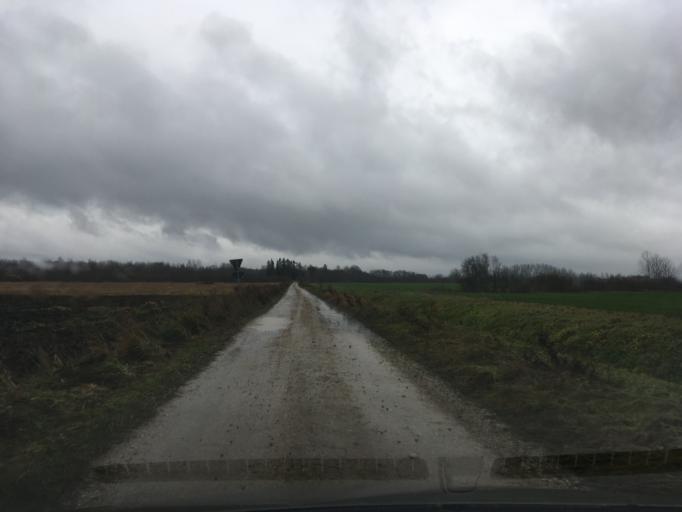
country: EE
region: Laeaene
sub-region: Lihula vald
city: Lihula
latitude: 58.7045
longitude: 23.8541
